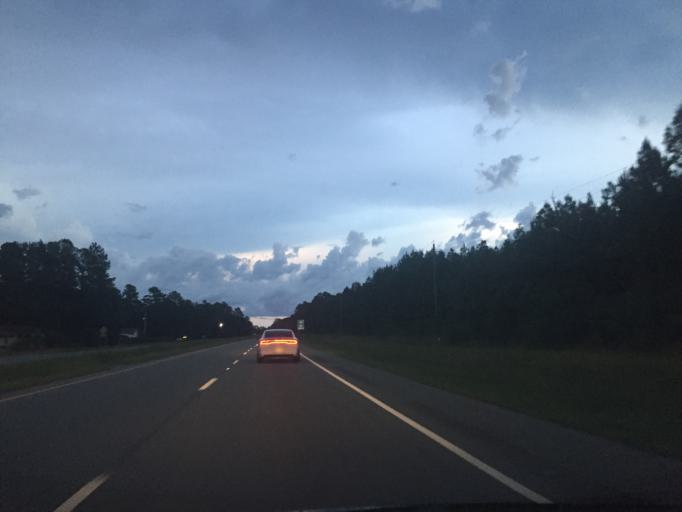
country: US
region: Georgia
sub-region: Liberty County
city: Midway
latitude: 31.8266
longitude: -81.5081
